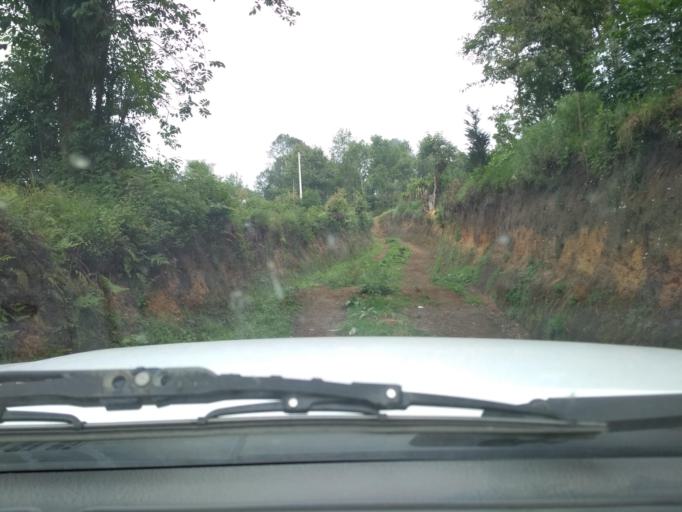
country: MX
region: Veracruz
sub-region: La Perla
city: Chilapa
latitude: 18.9911
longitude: -97.1668
